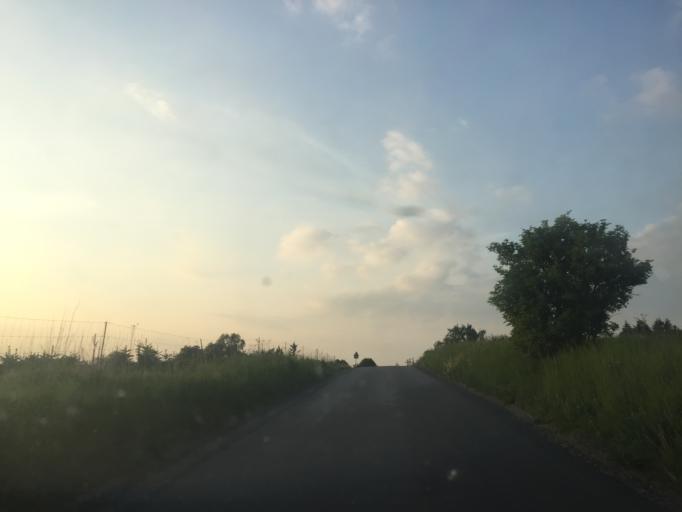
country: DK
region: South Denmark
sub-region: Odense Kommune
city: Bellinge
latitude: 55.3790
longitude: 10.3102
